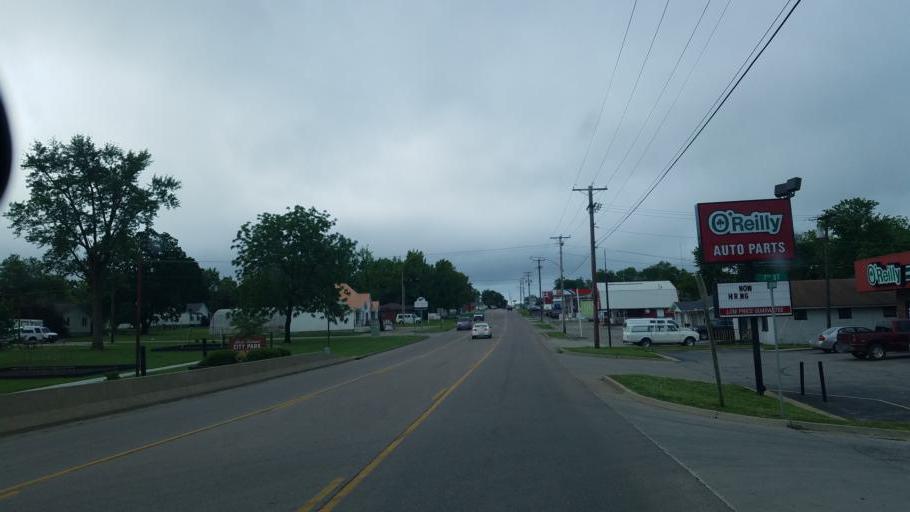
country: US
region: Missouri
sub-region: Miller County
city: Eldon
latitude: 38.3448
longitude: -92.5816
